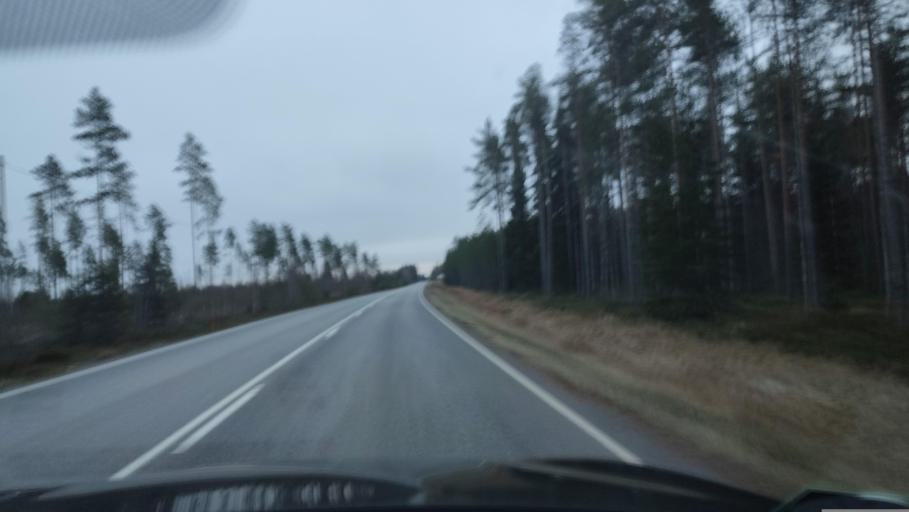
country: FI
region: Southern Ostrobothnia
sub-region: Suupohja
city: Kauhajoki
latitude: 62.3449
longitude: 21.9697
